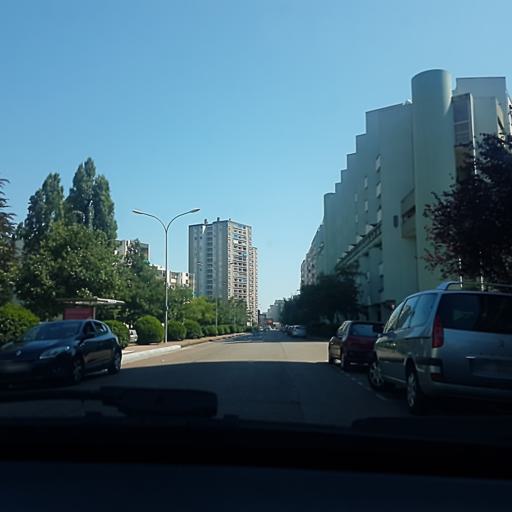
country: FR
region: Bourgogne
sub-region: Departement de Saone-et-Loire
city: Chalon-sur-Saone
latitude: 46.7882
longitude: 4.8422
